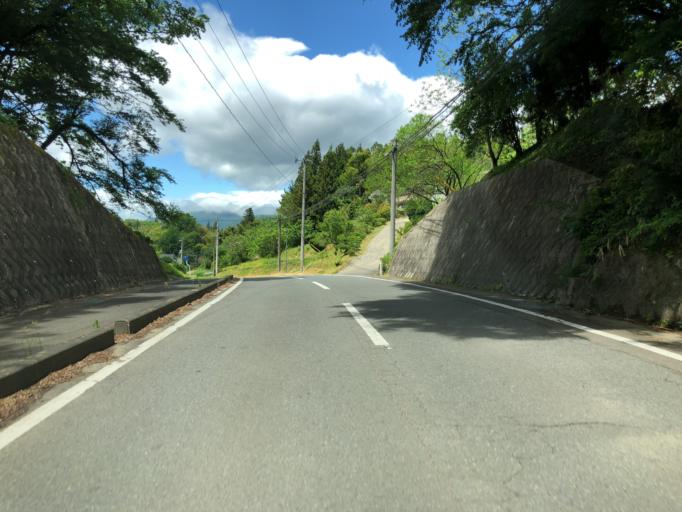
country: JP
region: Fukushima
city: Nihommatsu
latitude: 37.5548
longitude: 140.4659
